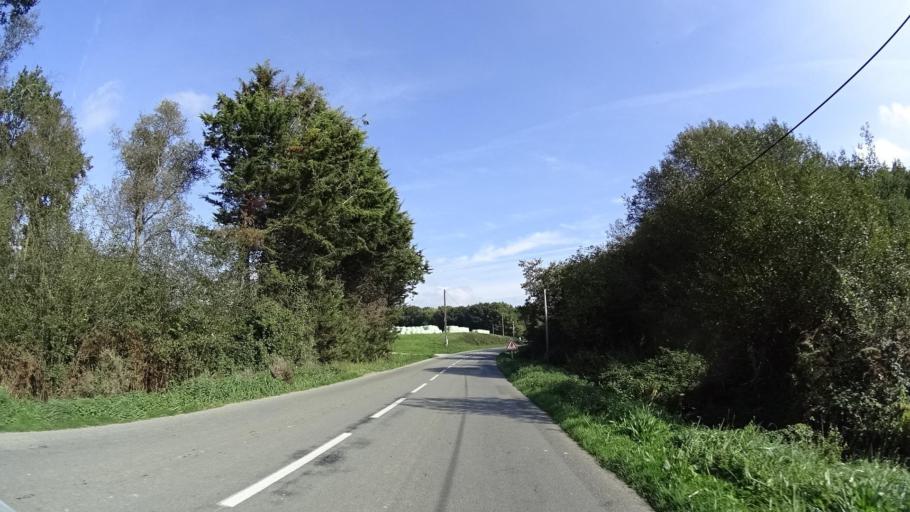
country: FR
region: Brittany
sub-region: Departement d'Ille-et-Vilaine
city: Medreac
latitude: 48.2747
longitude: -2.0329
